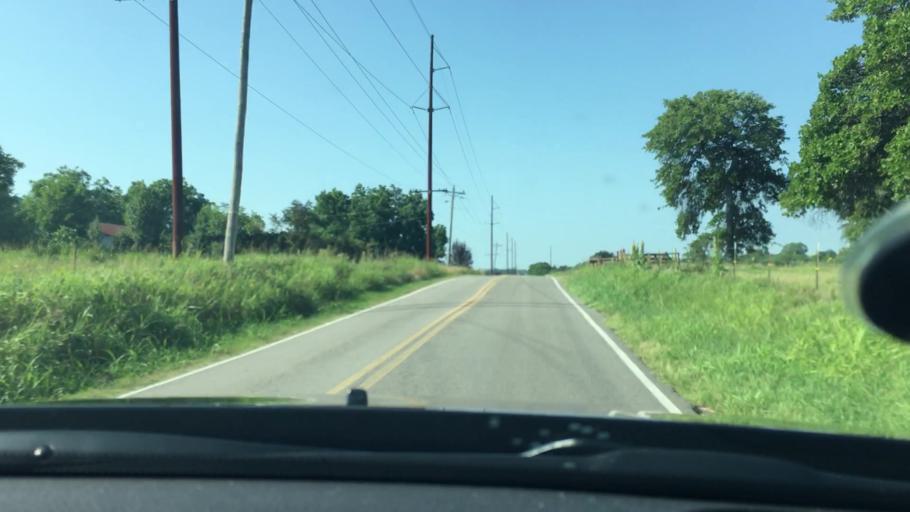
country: US
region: Oklahoma
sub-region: Pontotoc County
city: Ada
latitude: 34.8023
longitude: -96.6348
